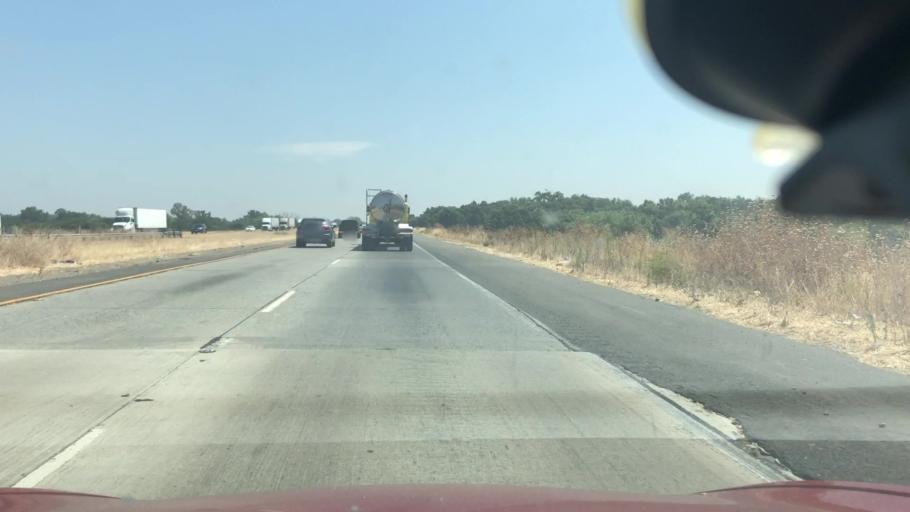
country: US
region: California
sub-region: San Joaquin County
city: Thornton
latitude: 38.2688
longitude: -121.4535
